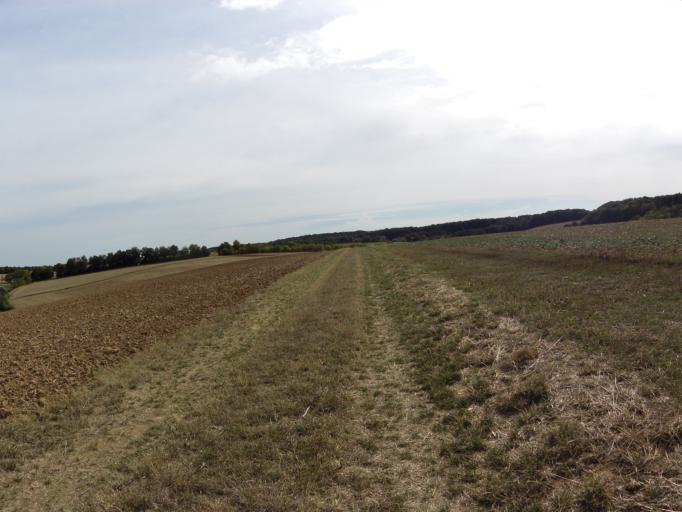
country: DE
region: Bavaria
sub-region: Regierungsbezirk Unterfranken
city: Waldbuttelbrunn
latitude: 49.7785
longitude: 9.8315
